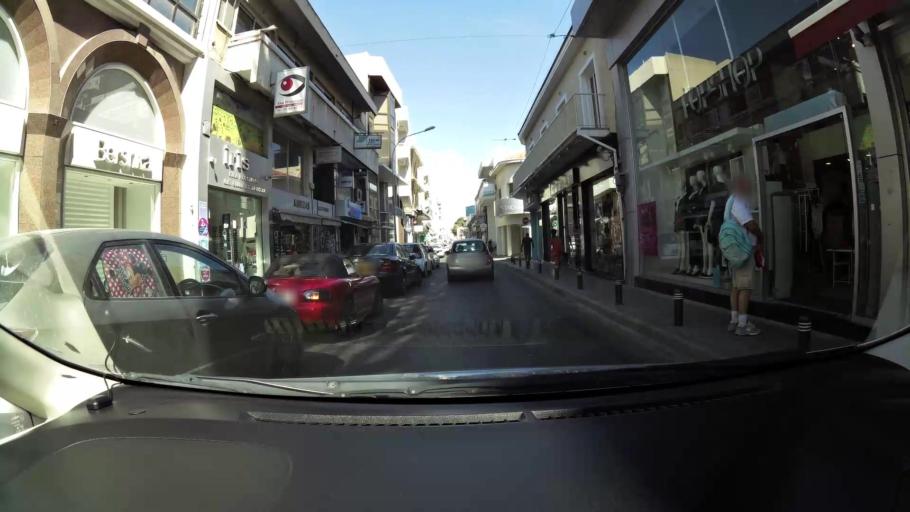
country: CY
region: Larnaka
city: Larnaca
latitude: 34.9138
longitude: 33.6364
